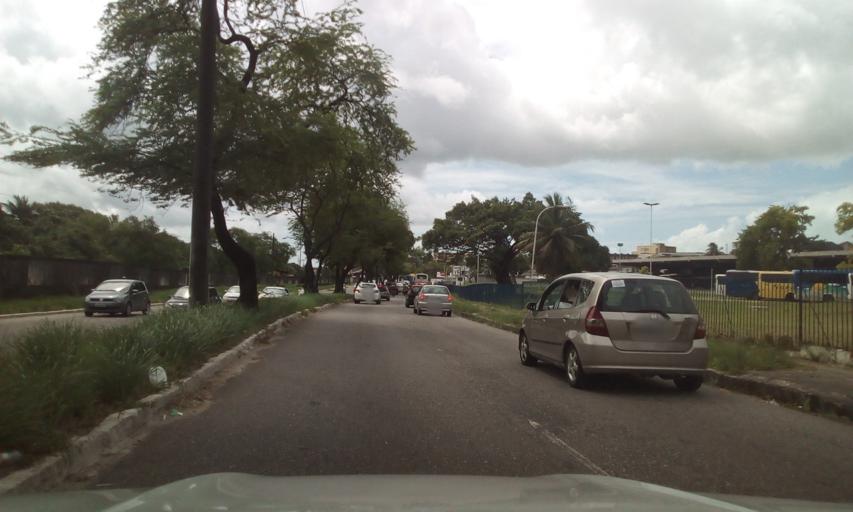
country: BR
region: Paraiba
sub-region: Joao Pessoa
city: Joao Pessoa
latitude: -7.1188
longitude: -34.8923
